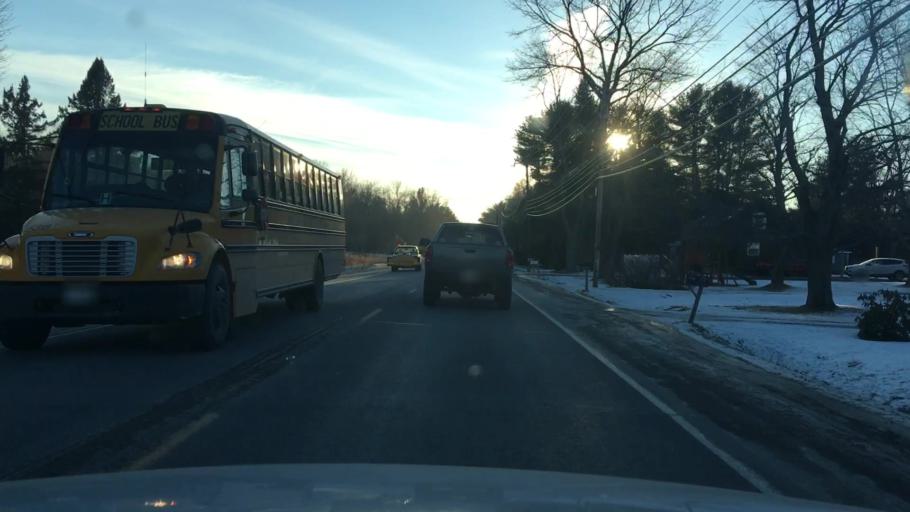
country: US
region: Maine
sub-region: Penobscot County
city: Brewer
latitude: 44.8112
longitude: -68.7351
